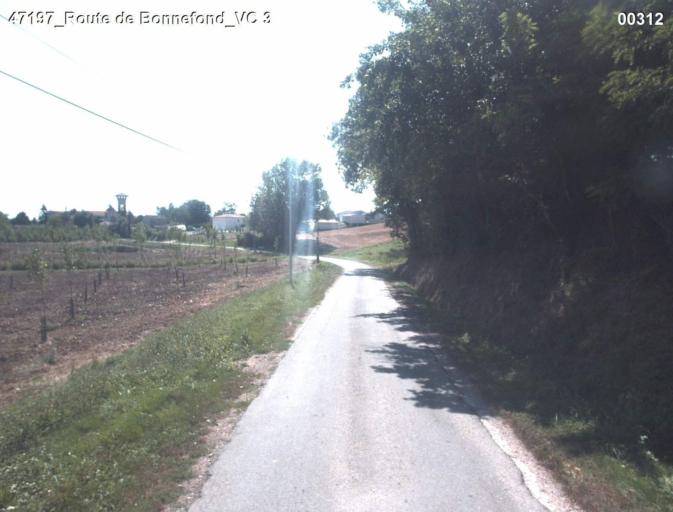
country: FR
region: Aquitaine
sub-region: Departement du Lot-et-Garonne
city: Laplume
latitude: 44.0981
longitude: 0.4754
